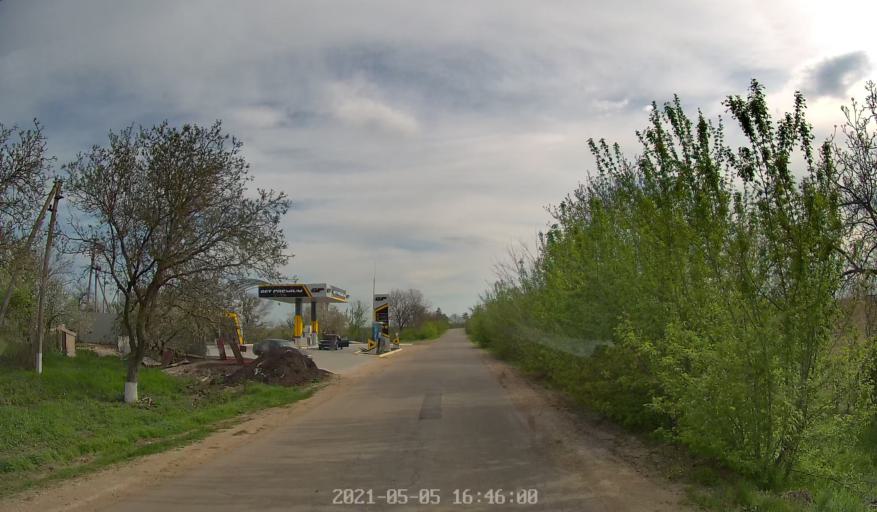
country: MD
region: Criuleni
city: Criuleni
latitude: 47.1041
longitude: 29.1924
